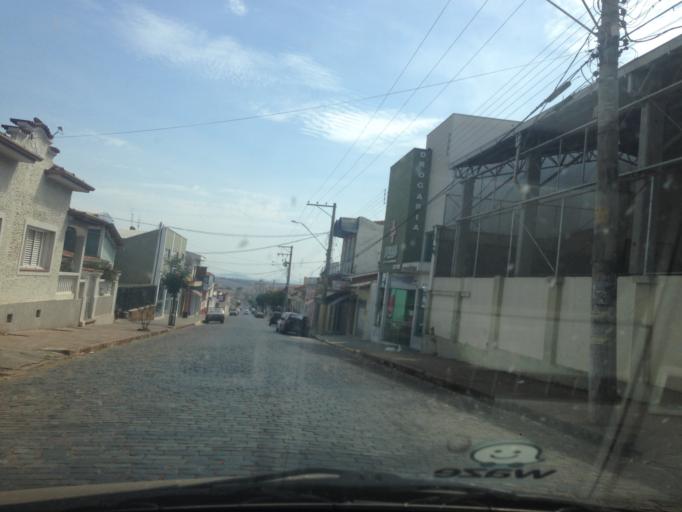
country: BR
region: Sao Paulo
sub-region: Casa Branca
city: Casa Branca
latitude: -21.7790
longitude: -47.0786
